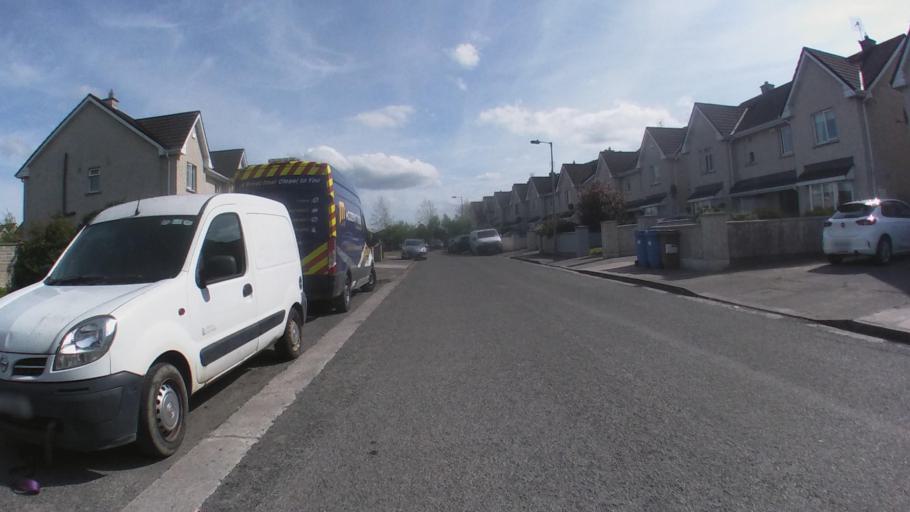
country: IE
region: Leinster
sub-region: County Carlow
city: Carlow
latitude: 52.8350
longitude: -6.9477
